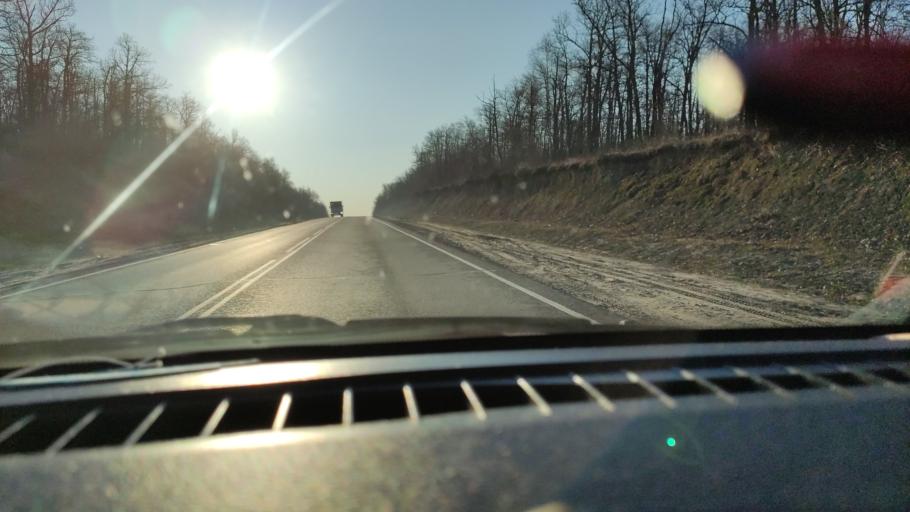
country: RU
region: Saratov
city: Vol'sk
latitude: 52.1081
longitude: 47.3963
